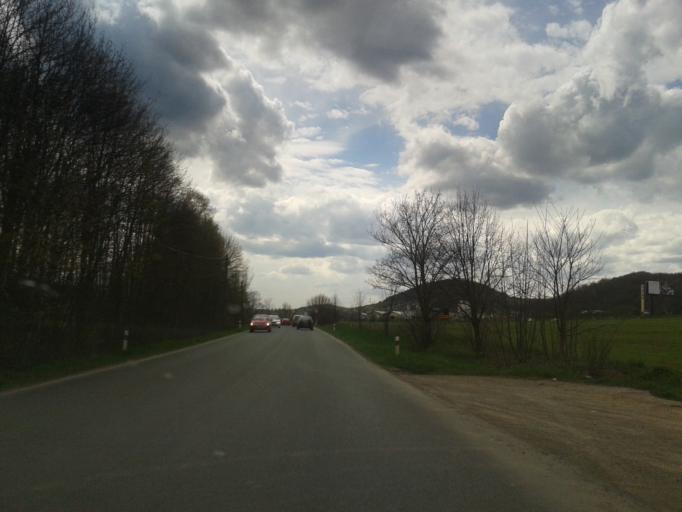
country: CZ
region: Central Bohemia
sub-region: Okres Beroun
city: Lodenice
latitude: 50.0042
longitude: 14.1751
